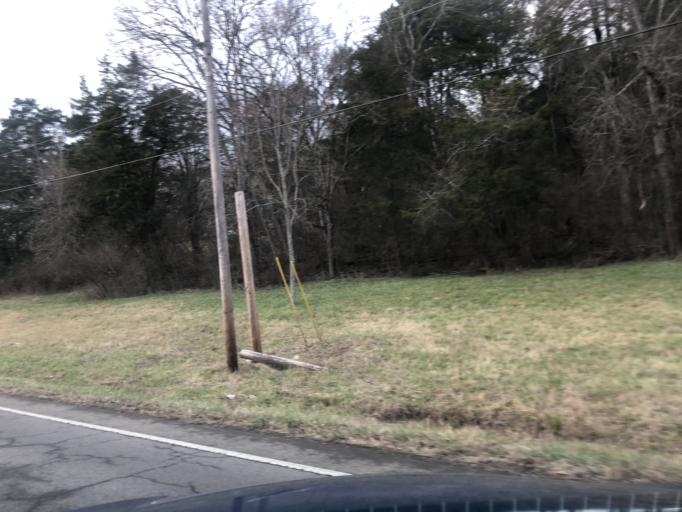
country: US
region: Tennessee
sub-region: Davidson County
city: Belle Meade
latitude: 36.1087
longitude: -86.9349
